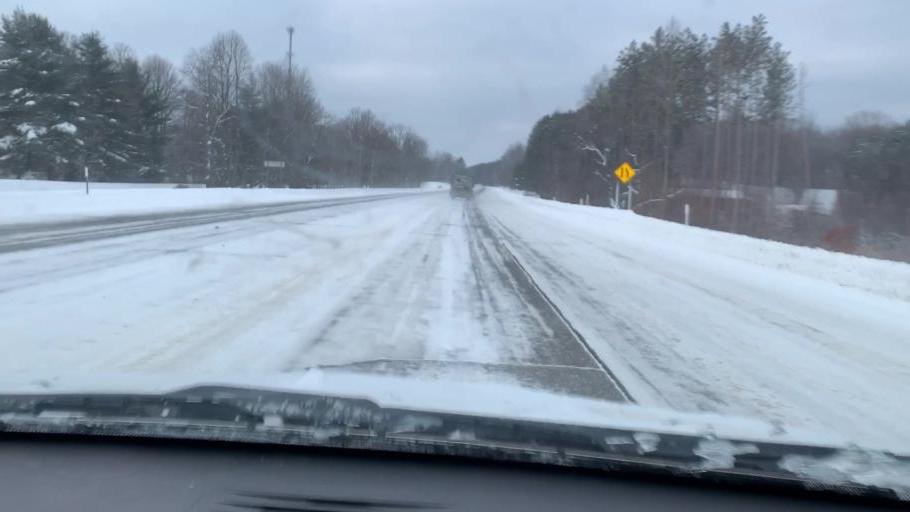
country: US
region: Michigan
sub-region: Kalkaska County
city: Kalkaska
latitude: 44.6104
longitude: -85.3134
